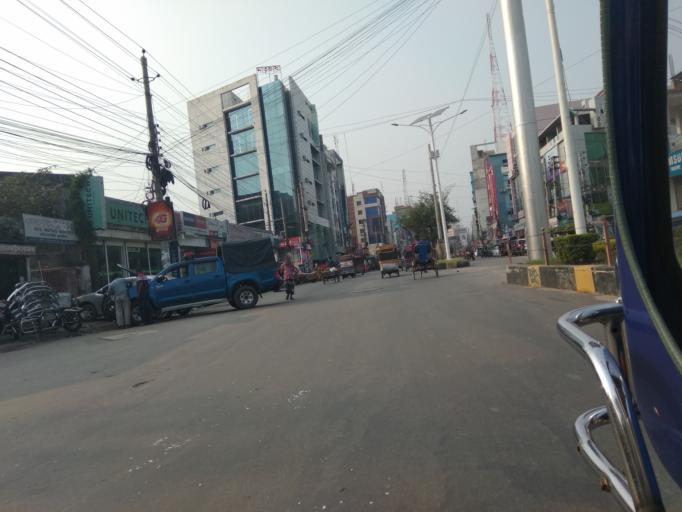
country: BD
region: Khulna
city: Khulna
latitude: 22.8175
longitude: 89.5535
